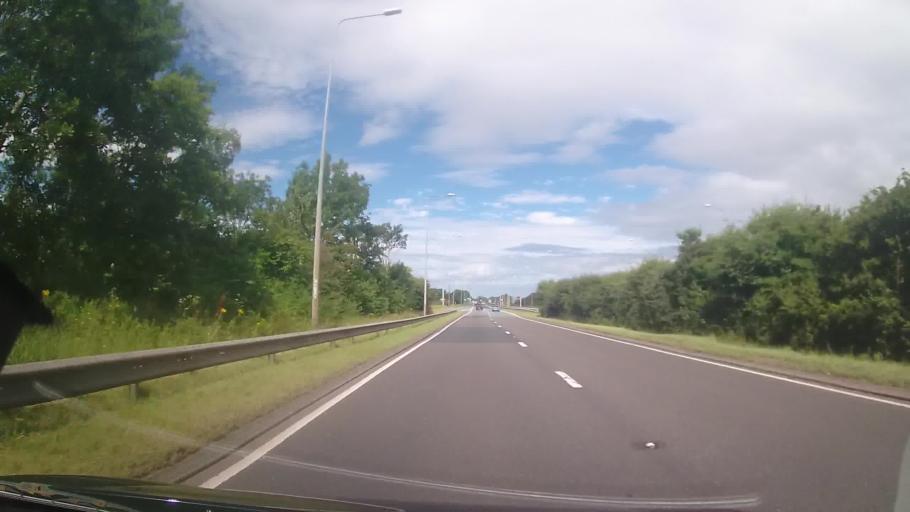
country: GB
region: Wales
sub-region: Denbighshire
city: Bodelwyddan
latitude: 53.2624
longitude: -3.4785
